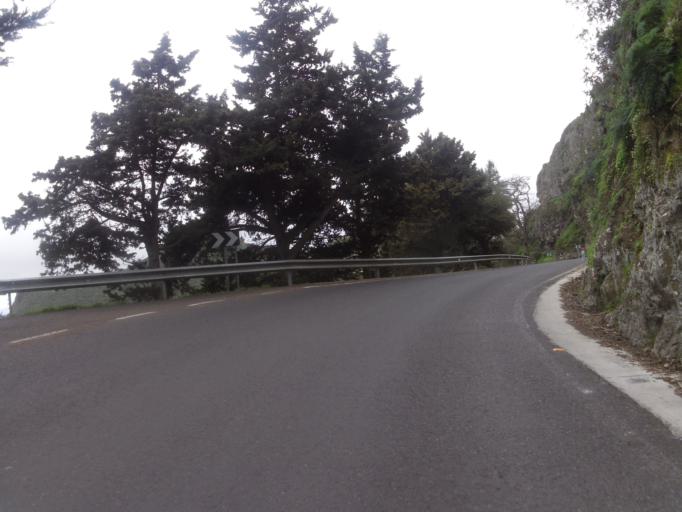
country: ES
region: Canary Islands
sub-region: Provincia de Las Palmas
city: Vega de San Mateo
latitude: 27.9993
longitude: -15.5321
